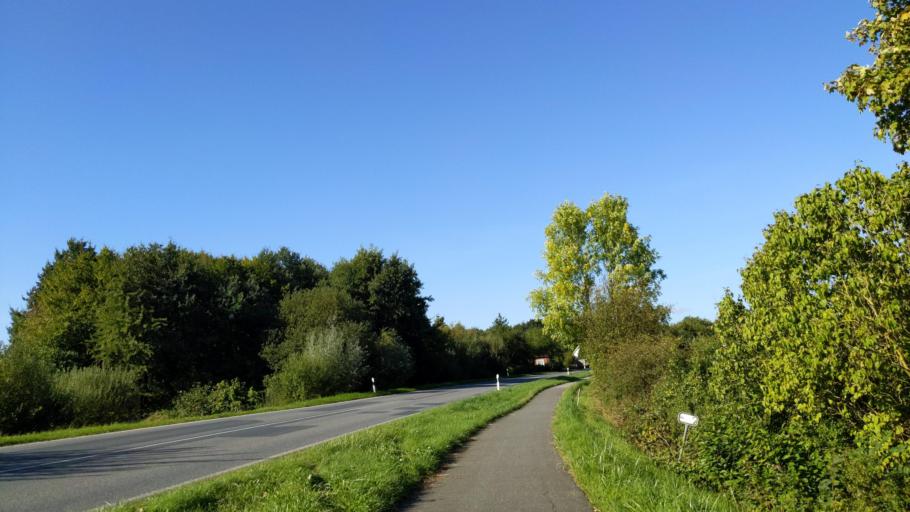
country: DE
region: Schleswig-Holstein
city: Ahrensbok
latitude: 53.9771
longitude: 10.5876
